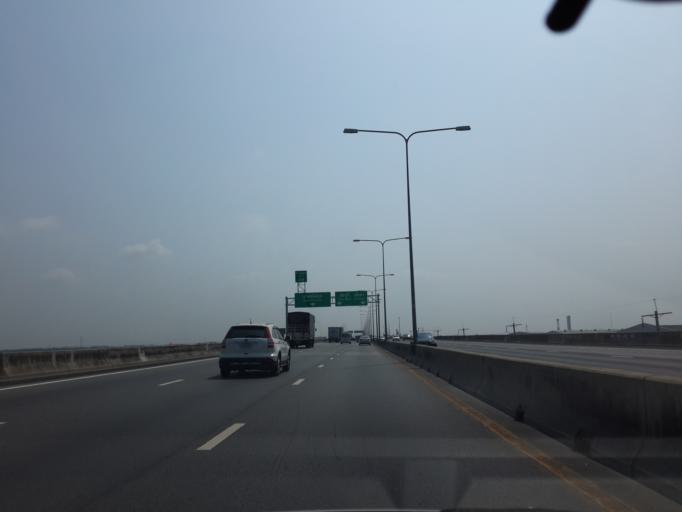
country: TH
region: Samut Prakan
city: Bang Bo
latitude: 13.5770
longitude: 100.8886
